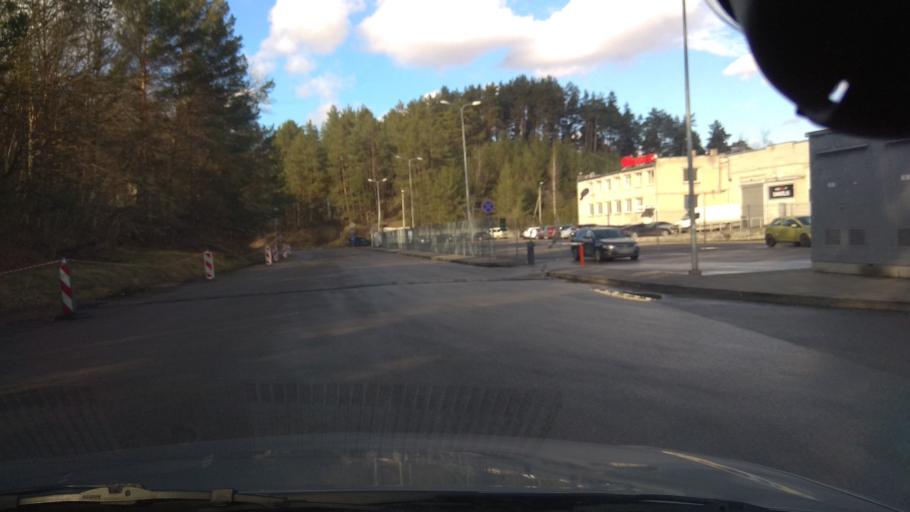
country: LT
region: Vilnius County
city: Lazdynai
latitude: 54.6434
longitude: 25.2224
